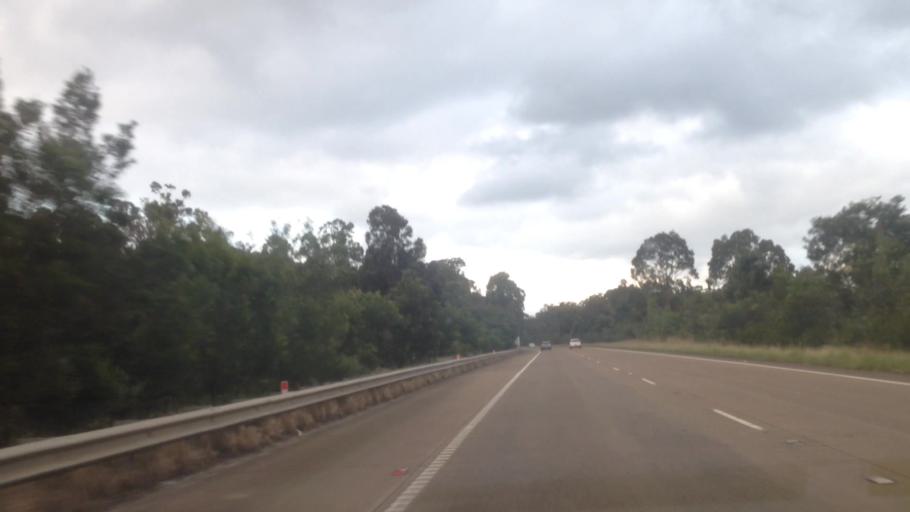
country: AU
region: New South Wales
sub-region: Lake Macquarie Shire
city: Dora Creek
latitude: -33.1486
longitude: 151.4738
